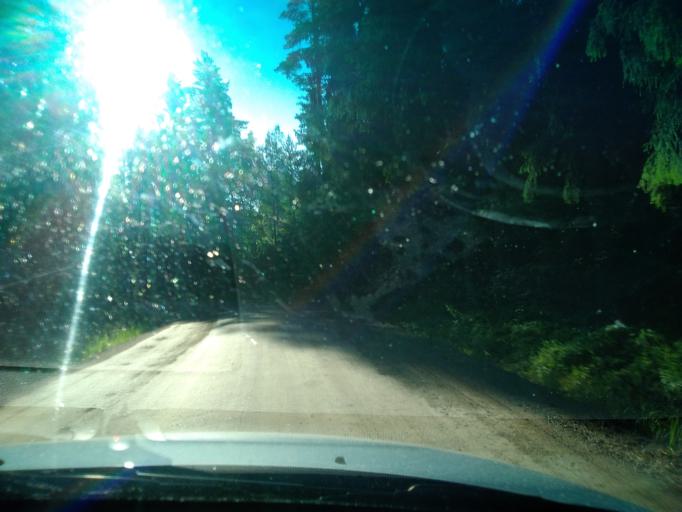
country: FI
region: Haeme
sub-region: Forssa
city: Tammela
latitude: 60.7562
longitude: 23.7608
